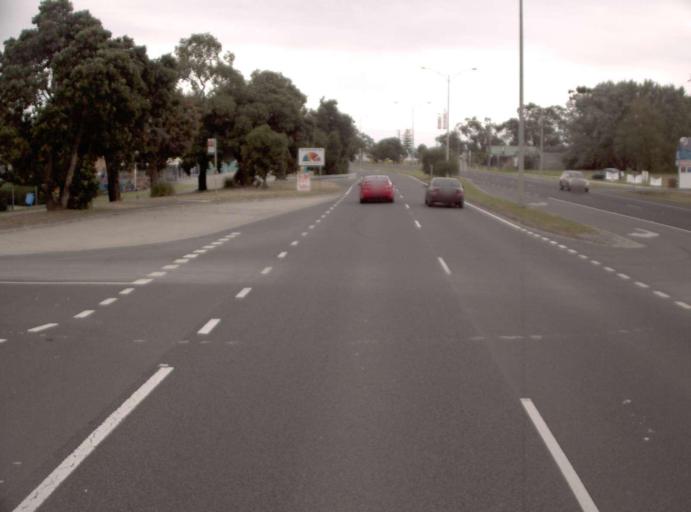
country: AU
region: Victoria
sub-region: Casey
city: Tooradin
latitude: -38.2102
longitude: 145.3774
